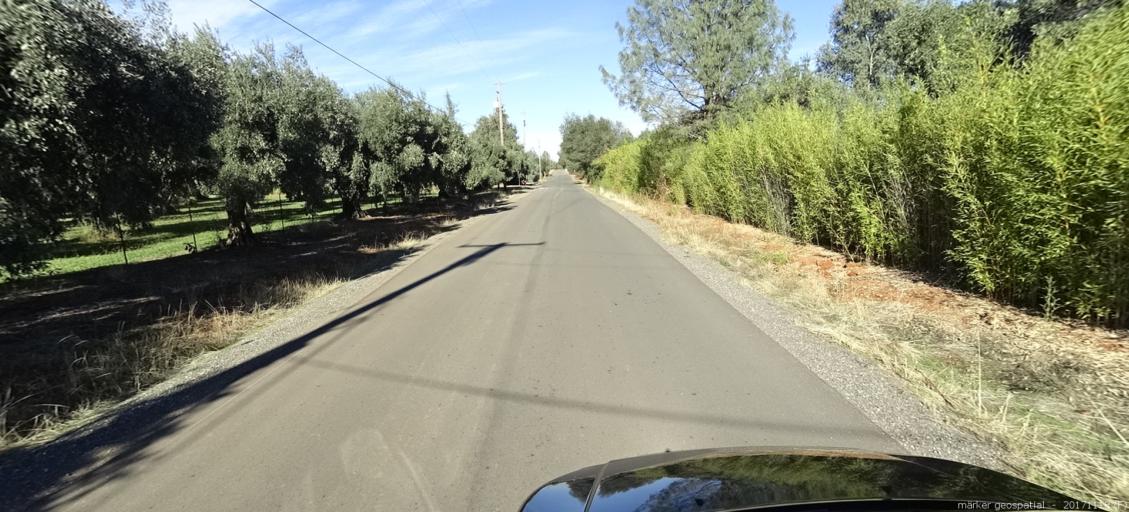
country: US
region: California
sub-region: Shasta County
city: Anderson
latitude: 40.4484
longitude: -122.4357
